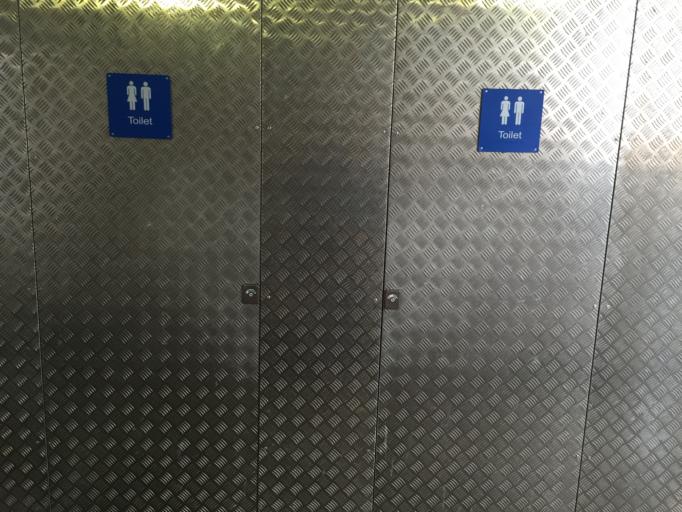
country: AU
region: New South Wales
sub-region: Snowy River
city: Jindabyne
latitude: -36.4573
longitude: 148.2694
